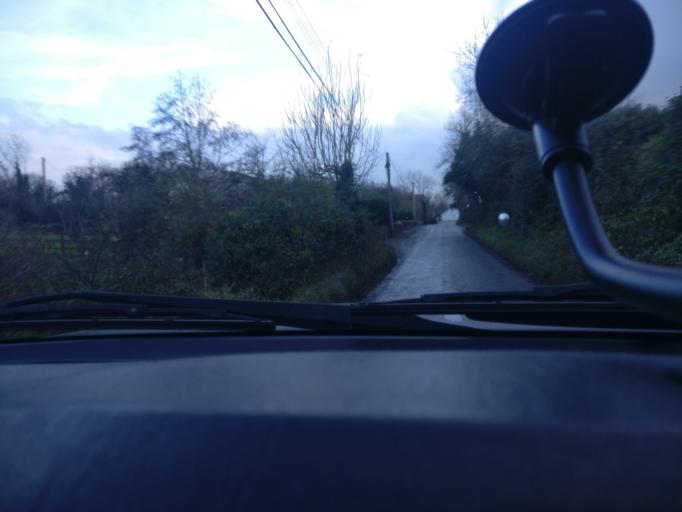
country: IE
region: Connaught
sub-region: County Galway
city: Athenry
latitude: 53.2075
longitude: -8.7163
